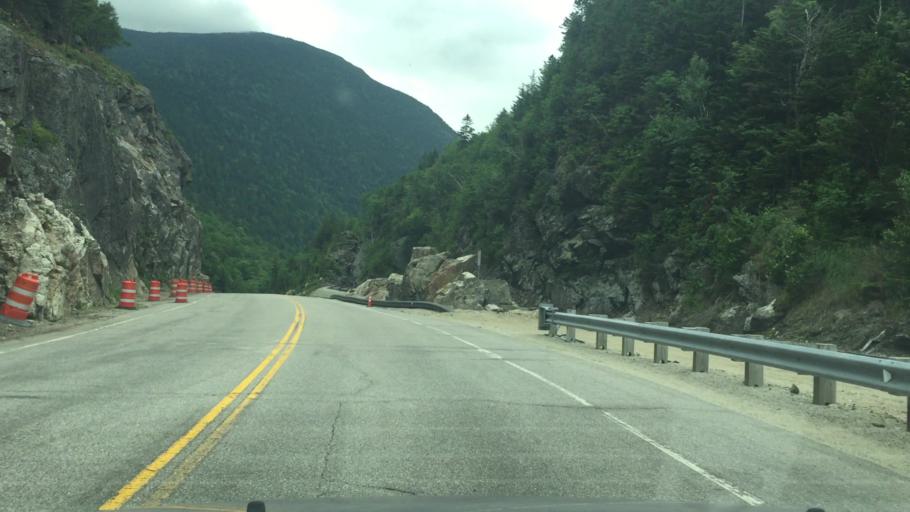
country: US
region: New Hampshire
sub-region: Grafton County
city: Deerfield
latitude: 44.2136
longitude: -71.4071
